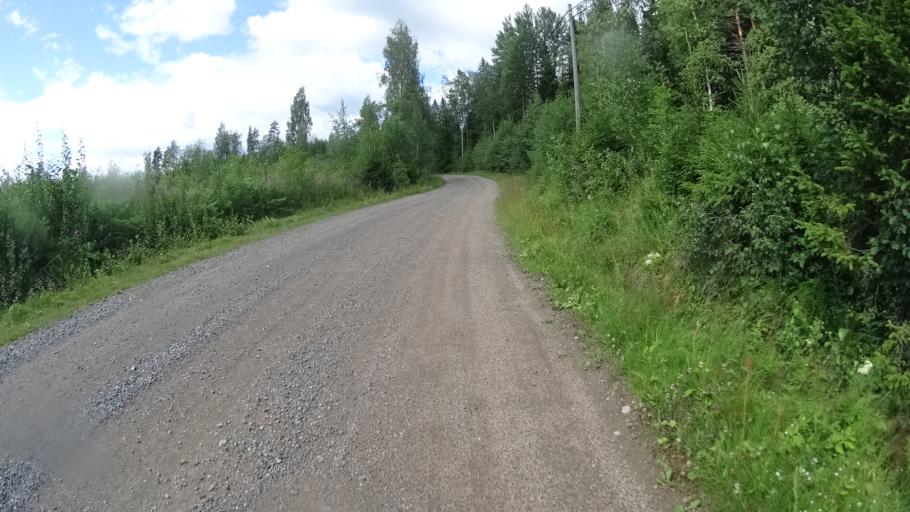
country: FI
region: Uusimaa
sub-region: Helsinki
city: Karkkila
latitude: 60.5971
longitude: 24.2175
